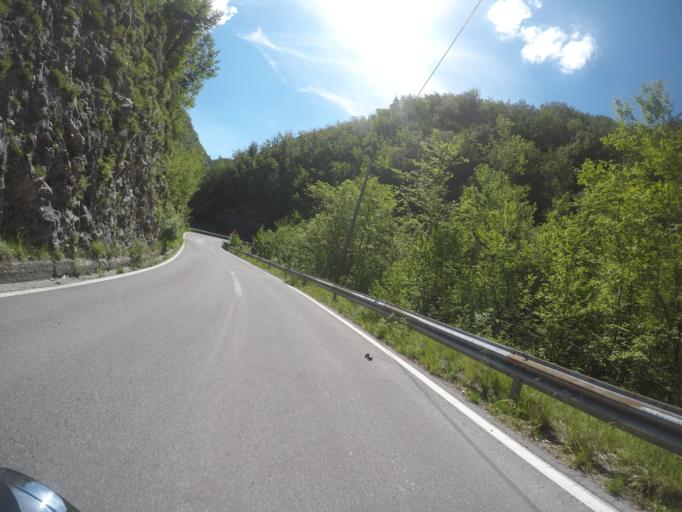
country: IT
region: Tuscany
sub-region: Provincia di Lucca
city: Fontana delle Monache
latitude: 44.0580
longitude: 10.2621
